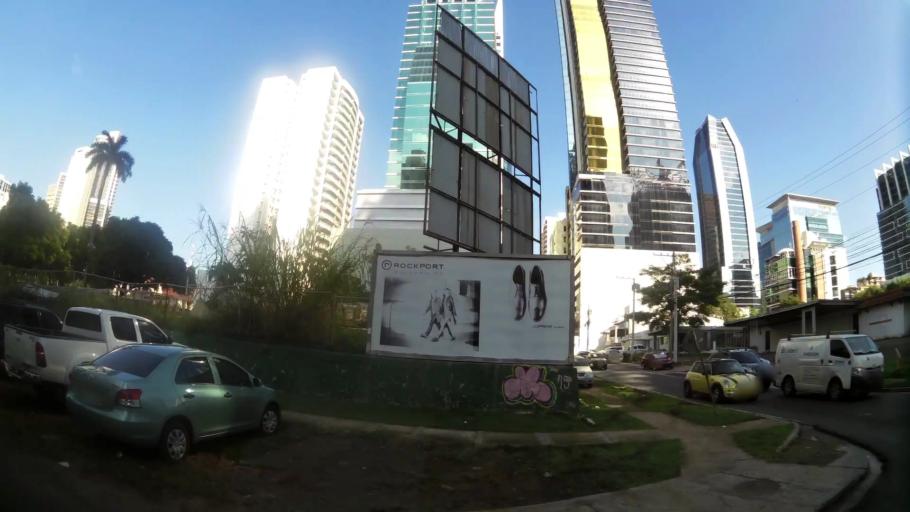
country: PA
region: Panama
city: Panama
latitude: 8.9838
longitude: -79.5207
